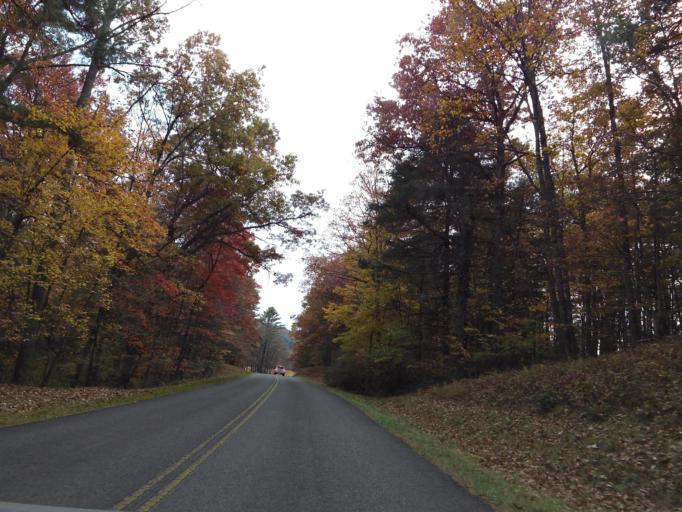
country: US
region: Virginia
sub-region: City of Galax
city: Galax
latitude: 36.5868
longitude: -80.8554
